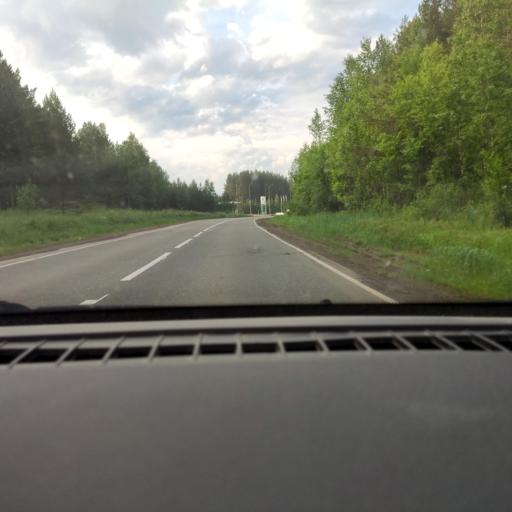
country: RU
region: Udmurtiya
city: Votkinsk
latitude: 57.1589
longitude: 54.1224
